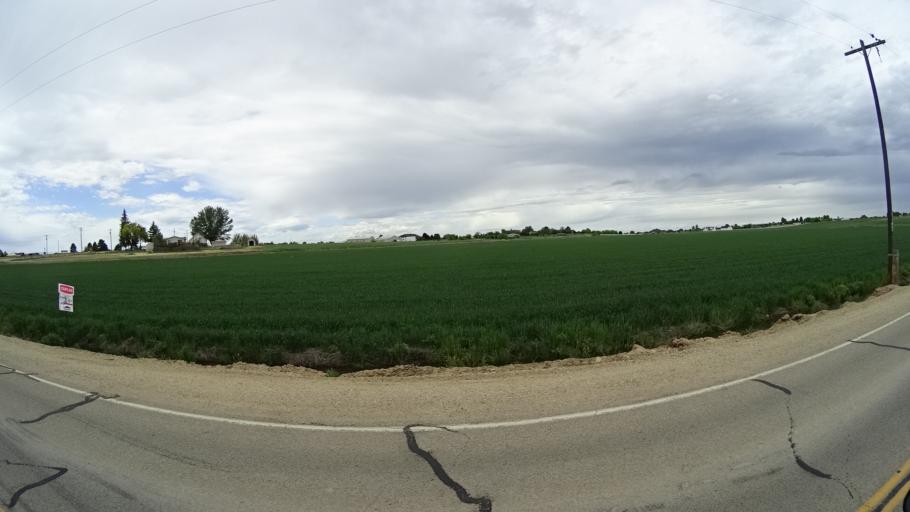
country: US
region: Idaho
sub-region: Ada County
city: Meridian
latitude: 43.5622
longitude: -116.4139
